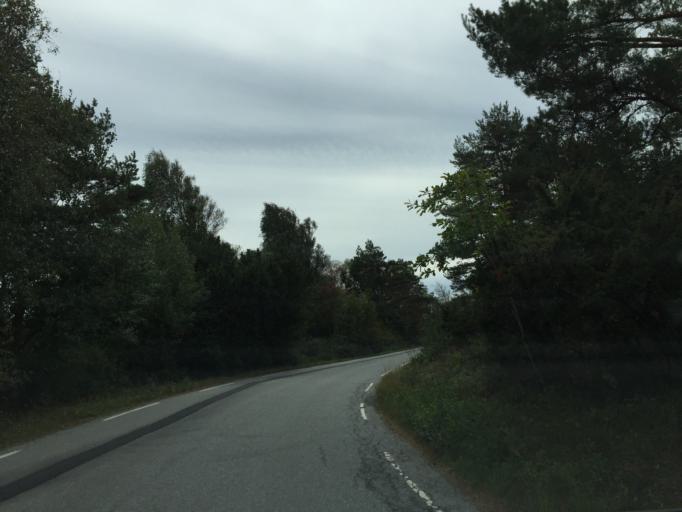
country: NO
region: Ostfold
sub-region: Hvaler
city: Skjaerhalden
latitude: 59.0455
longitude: 10.9540
